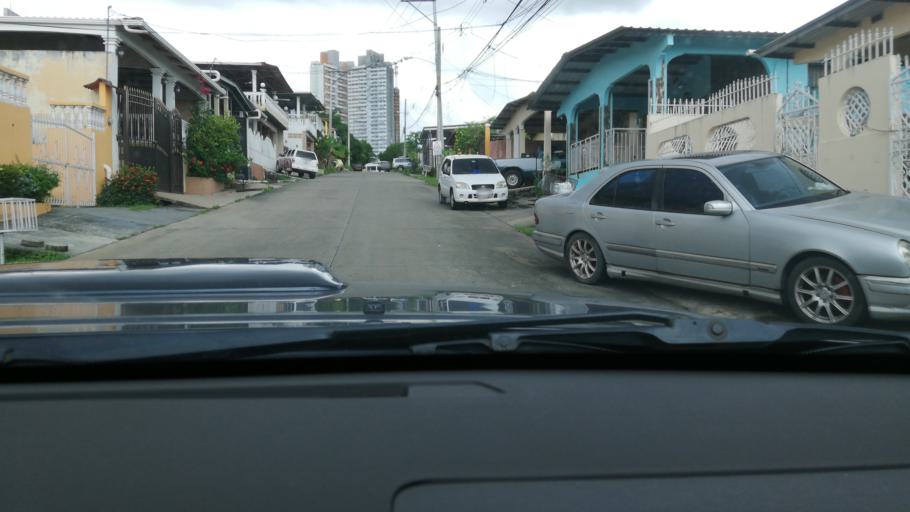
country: PA
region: Panama
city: San Miguelito
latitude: 9.0488
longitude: -79.4772
